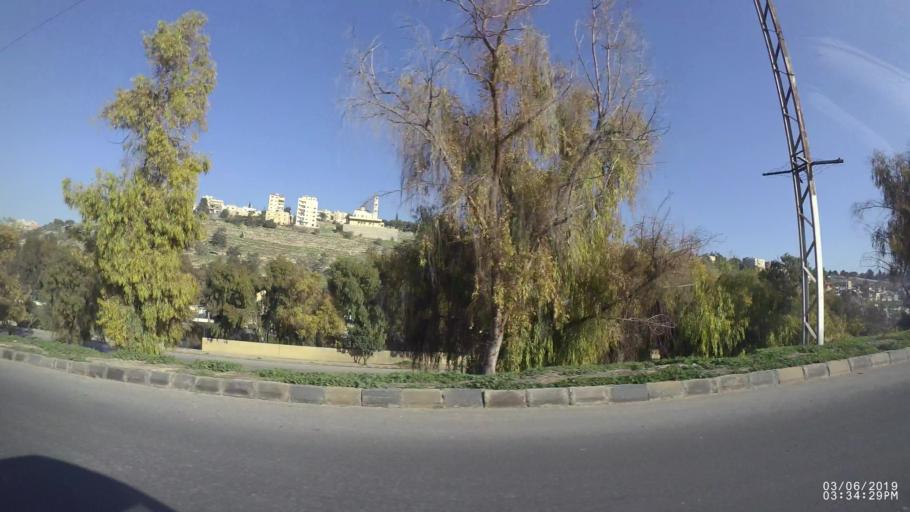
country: JO
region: Amman
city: Amman
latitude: 31.9769
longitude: 35.9707
